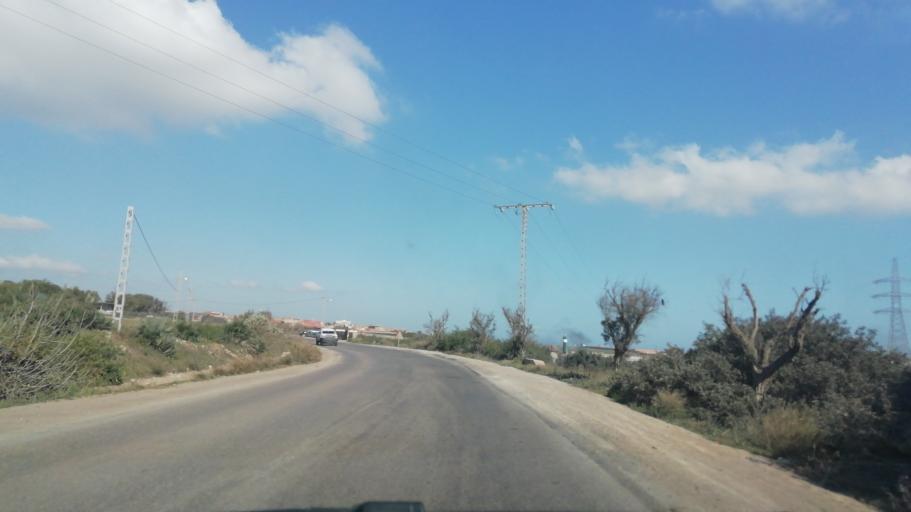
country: DZ
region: Oran
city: Ain el Bya
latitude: 35.7671
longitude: -0.2763
